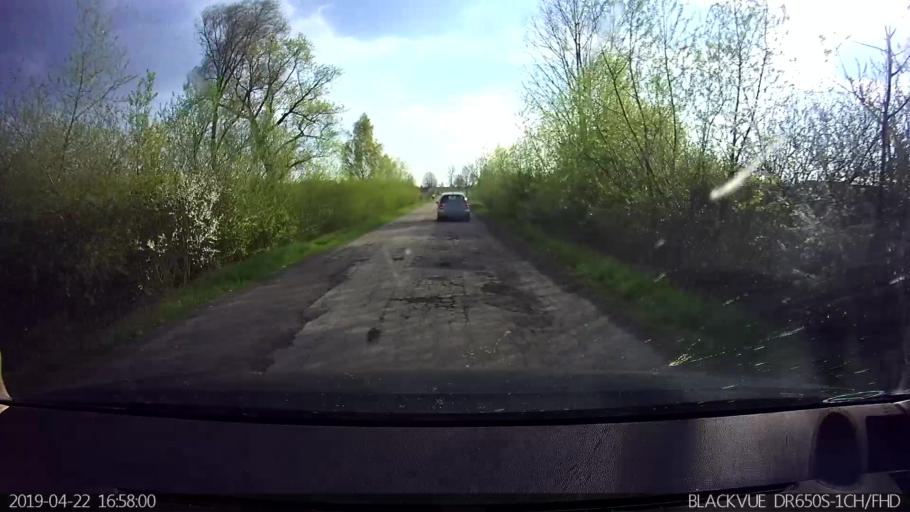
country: PL
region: Podlasie
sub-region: Powiat siemiatycki
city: Siemiatycze
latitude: 52.4742
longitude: 22.7543
